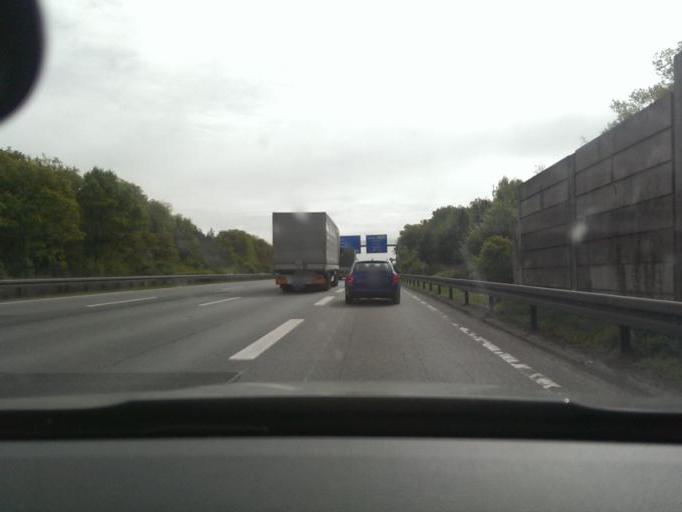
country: DE
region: Lower Saxony
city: Lehre
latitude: 52.3080
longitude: 10.7147
